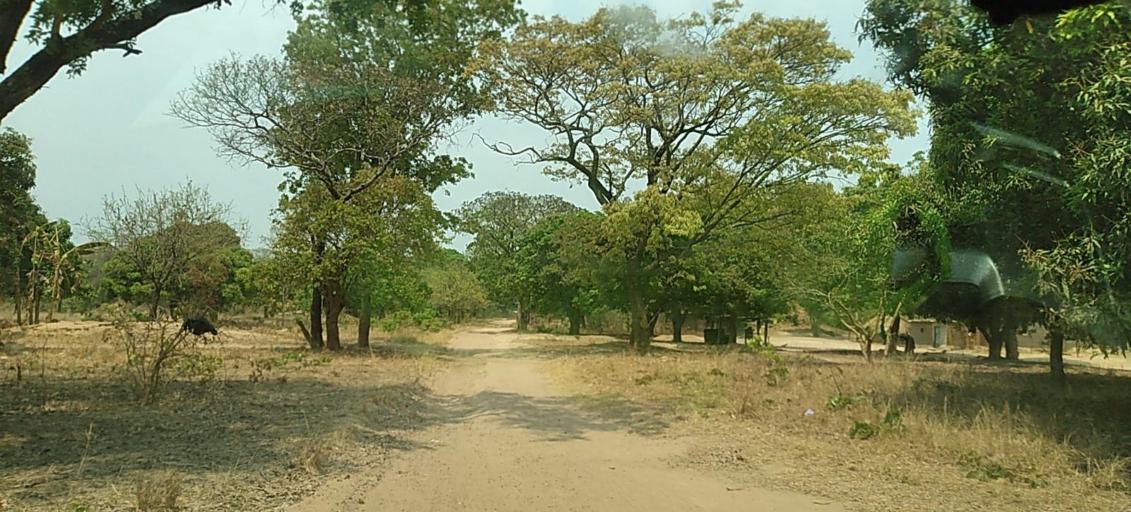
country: ZM
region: North-Western
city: Kabompo
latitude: -13.5606
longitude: 24.4460
